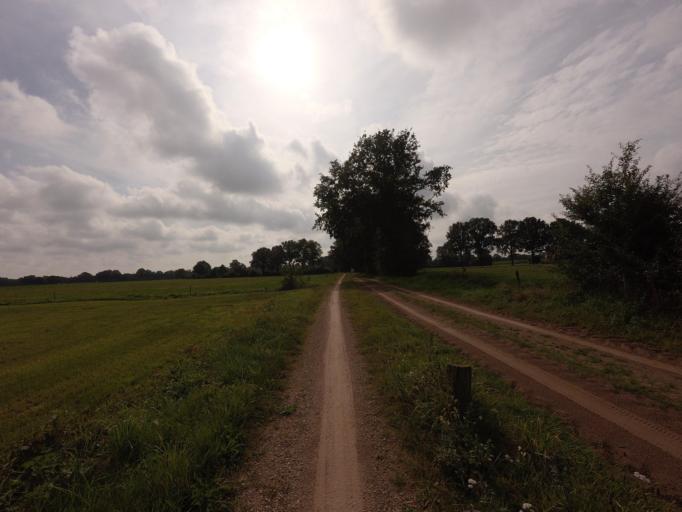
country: DE
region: Lower Saxony
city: Lage
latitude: 52.4253
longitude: 6.9517
